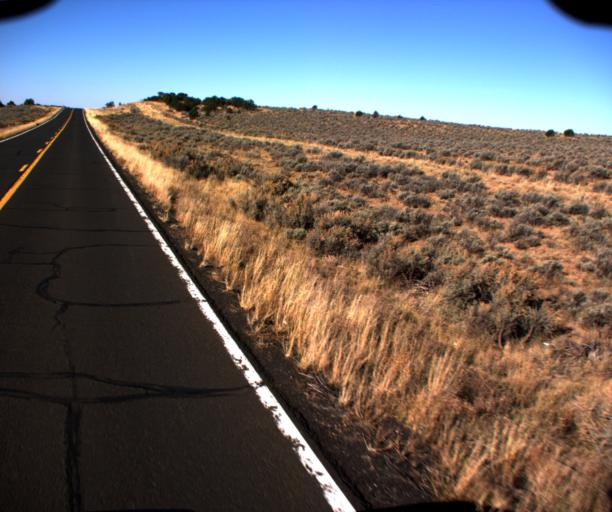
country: US
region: Arizona
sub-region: Navajo County
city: First Mesa
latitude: 35.7517
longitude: -110.0380
